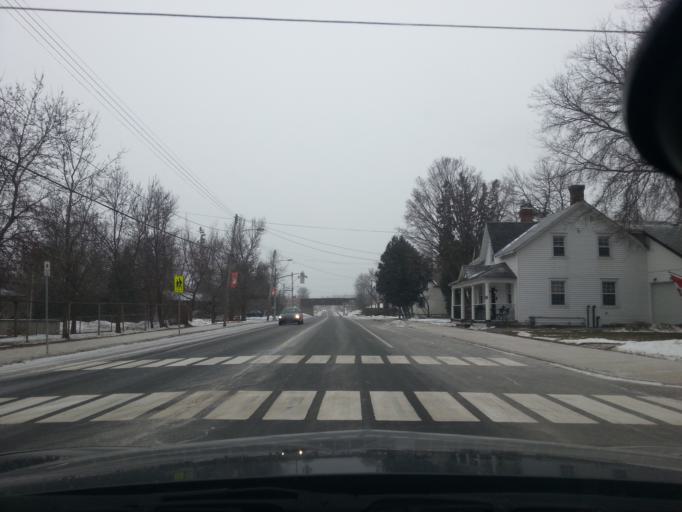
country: CA
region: Ontario
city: Arnprior
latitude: 45.3309
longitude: -76.2908
